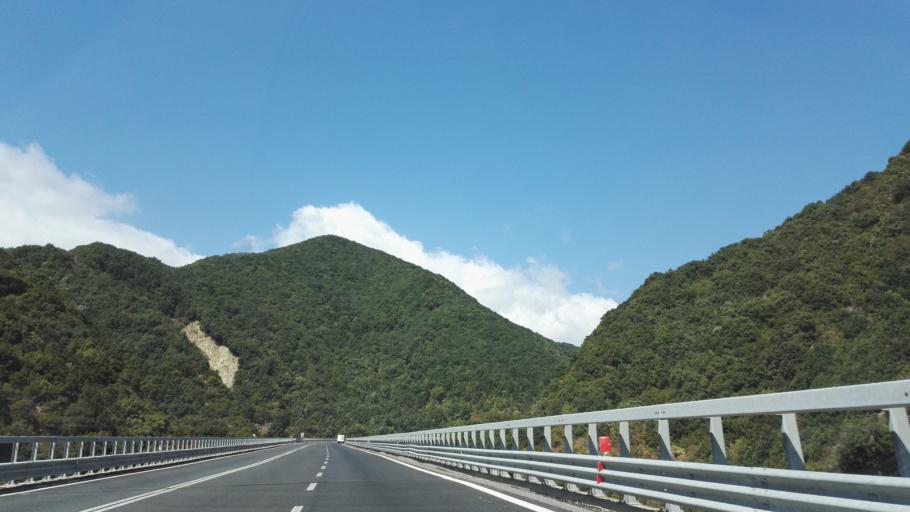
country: IT
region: Calabria
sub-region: Provincia di Reggio Calabria
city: Mammola
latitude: 38.3622
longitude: 16.1954
